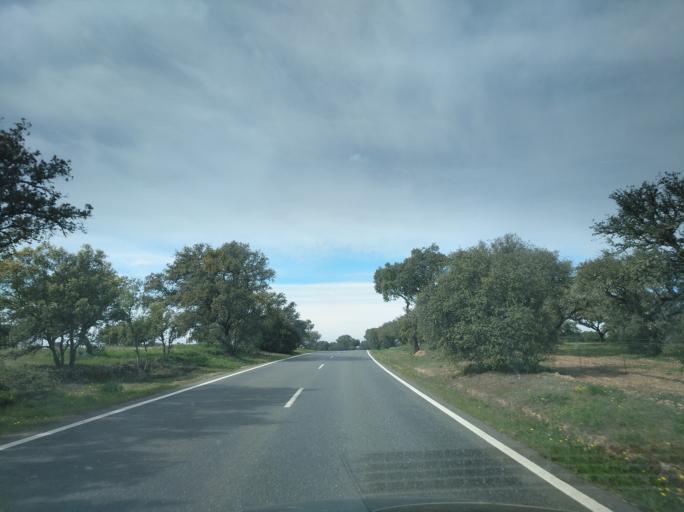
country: PT
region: Beja
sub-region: Mertola
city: Mertola
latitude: 37.7515
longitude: -7.8044
